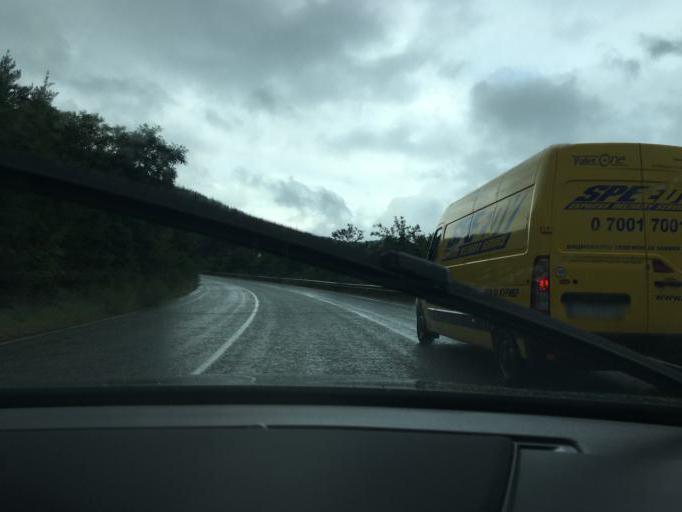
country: BG
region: Kyustendil
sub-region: Obshtina Kyustendil
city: Kyustendil
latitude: 42.2666
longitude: 22.5819
